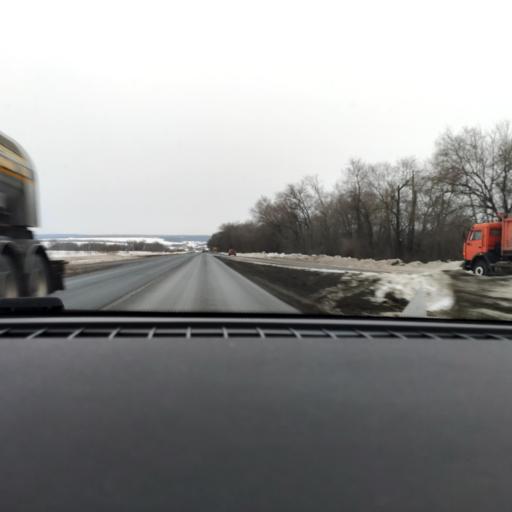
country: RU
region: Samara
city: Smyshlyayevka
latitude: 53.2647
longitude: 50.4710
